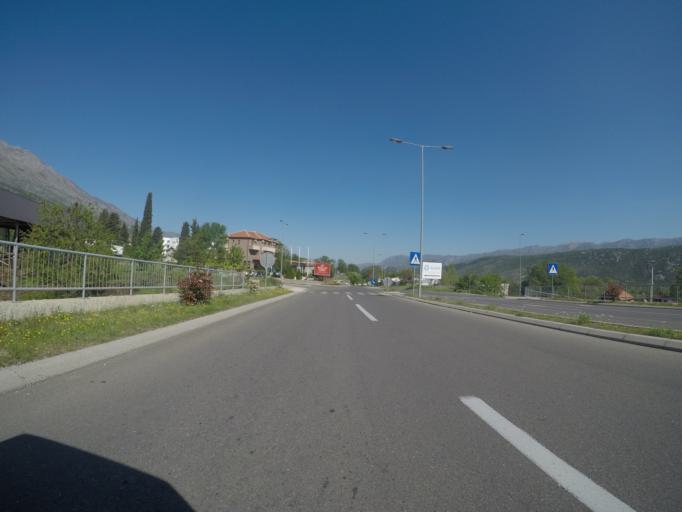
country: ME
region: Danilovgrad
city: Danilovgrad
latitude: 42.5533
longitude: 19.0894
